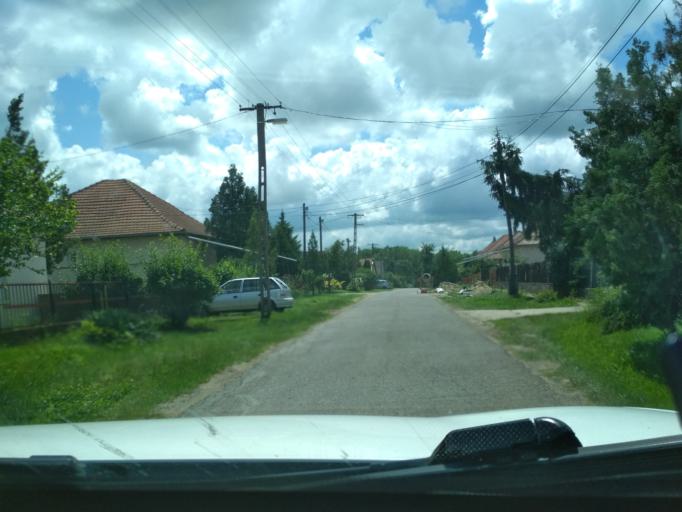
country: HU
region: Jasz-Nagykun-Szolnok
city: Tiszafured
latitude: 47.6070
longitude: 20.7771
